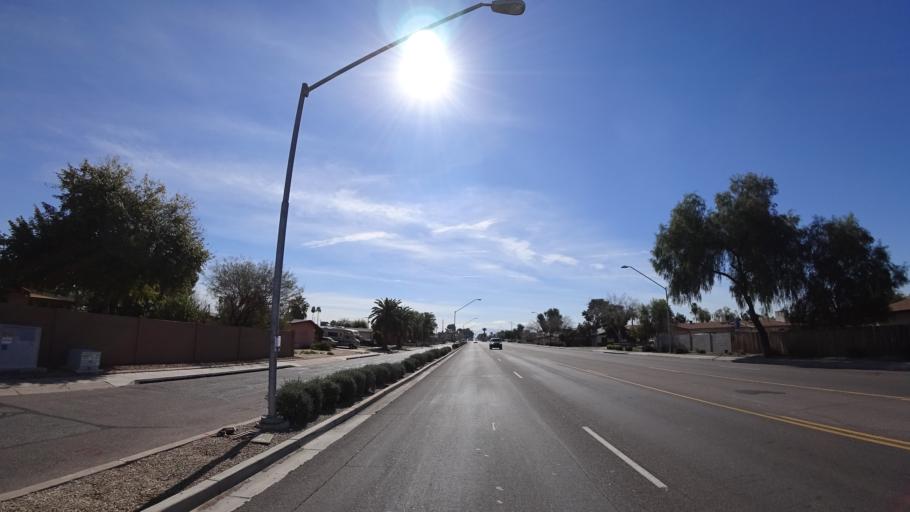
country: US
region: Arizona
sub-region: Maricopa County
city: Glendale
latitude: 33.5129
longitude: -112.2031
